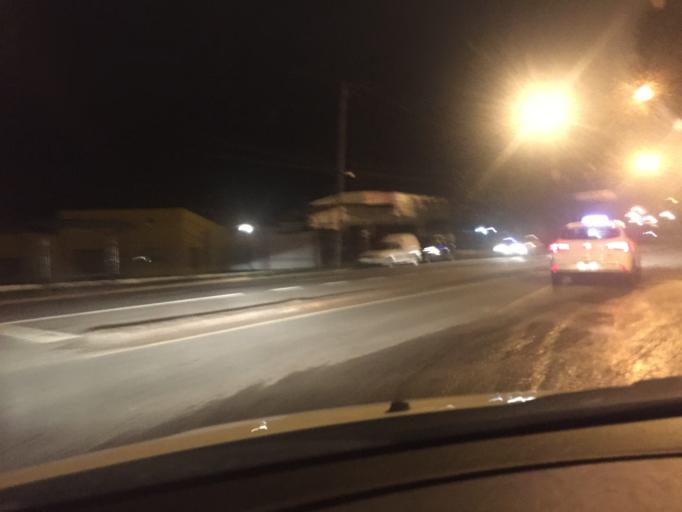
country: AR
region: Cordoba
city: Villa Allende
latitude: -31.3030
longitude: -64.2840
